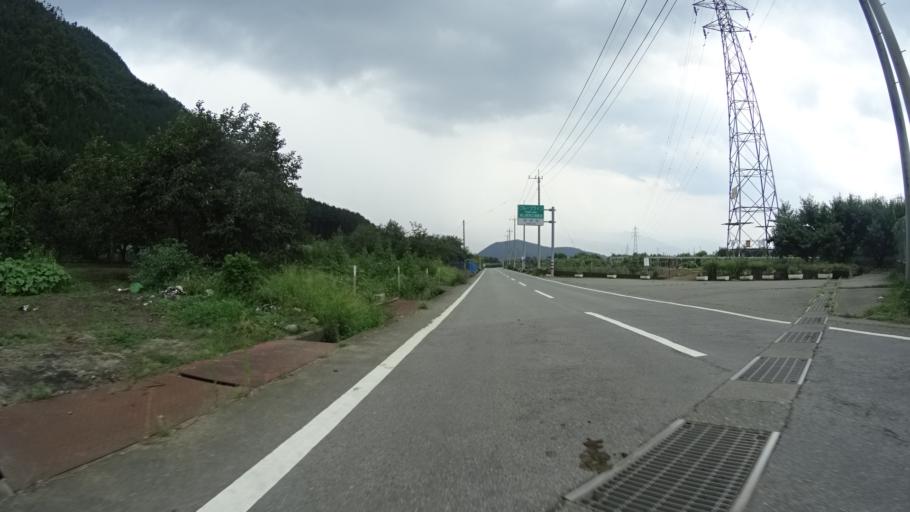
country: JP
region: Yamanashi
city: Enzan
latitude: 35.7355
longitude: 138.7218
